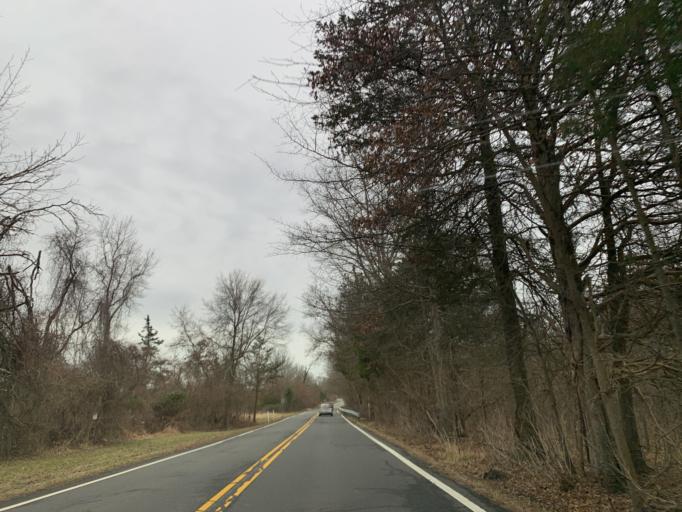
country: US
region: New Jersey
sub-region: Somerset County
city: Bridgewater
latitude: 40.6295
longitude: -74.7015
